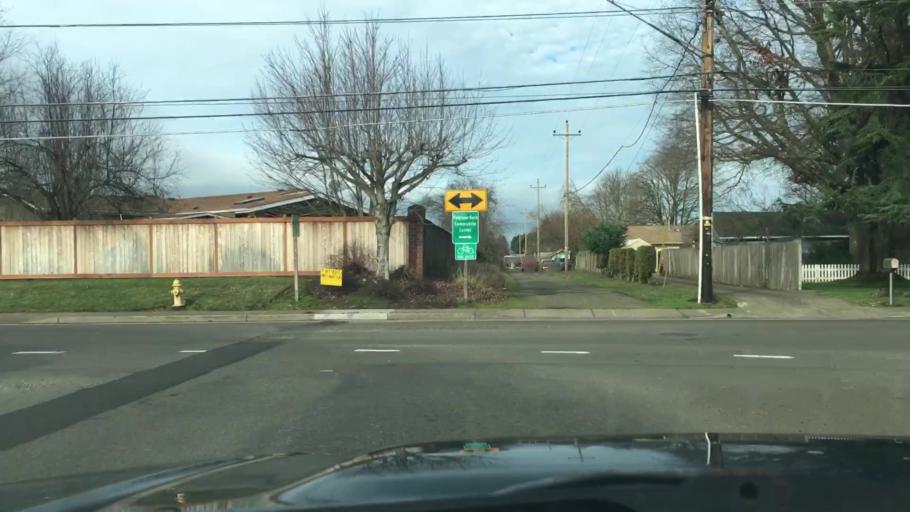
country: US
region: Oregon
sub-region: Lane County
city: Eugene
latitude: 44.0698
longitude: -123.1631
